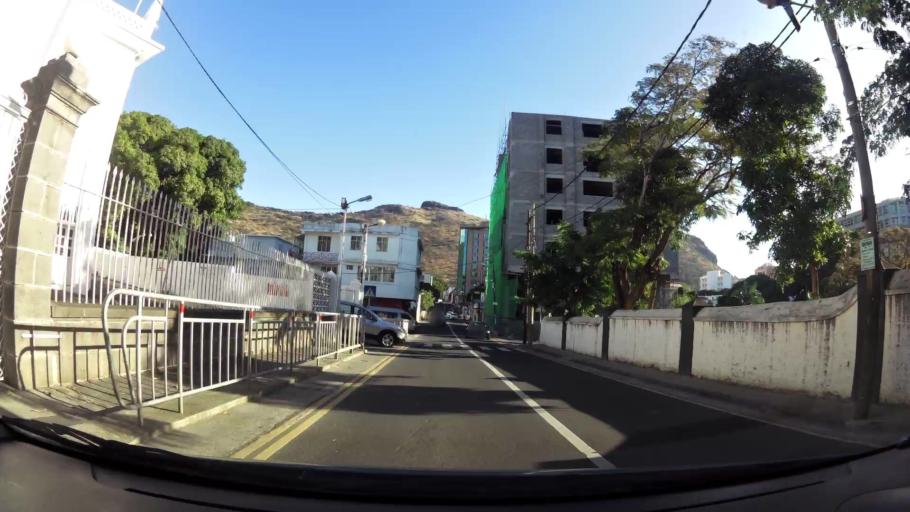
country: MU
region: Port Louis
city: Port Louis
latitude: -20.1681
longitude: 57.5060
